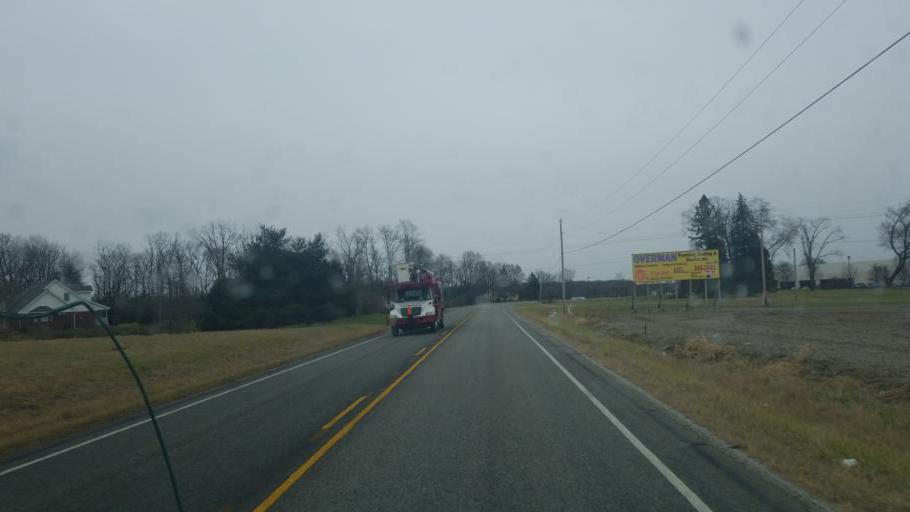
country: US
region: Indiana
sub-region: Henry County
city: Knightstown
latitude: 39.8238
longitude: -85.5357
